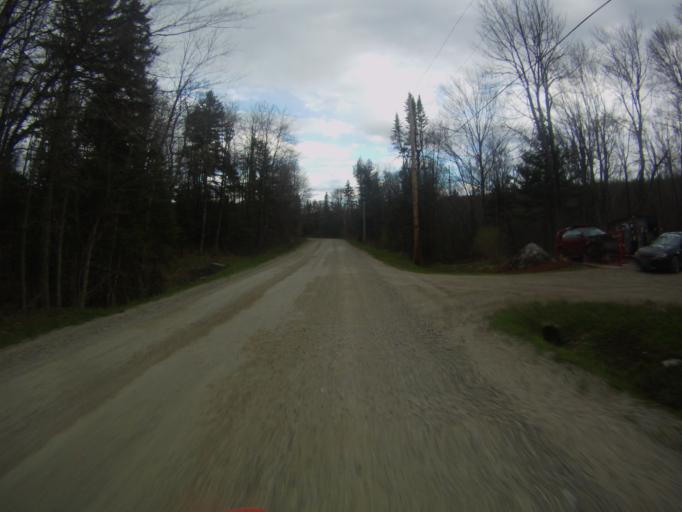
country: US
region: Vermont
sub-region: Addison County
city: Bristol
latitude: 44.0244
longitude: -73.0229
